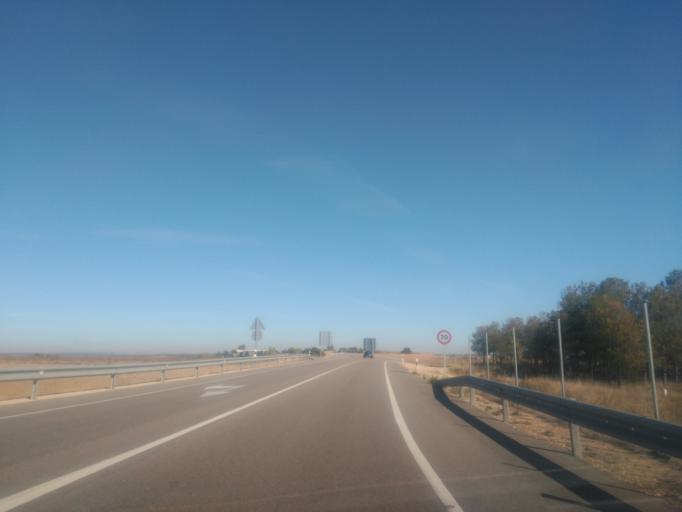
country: ES
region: Castille and Leon
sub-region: Provincia de Burgos
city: Castrillo de la Vega
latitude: 41.6377
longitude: -3.7816
